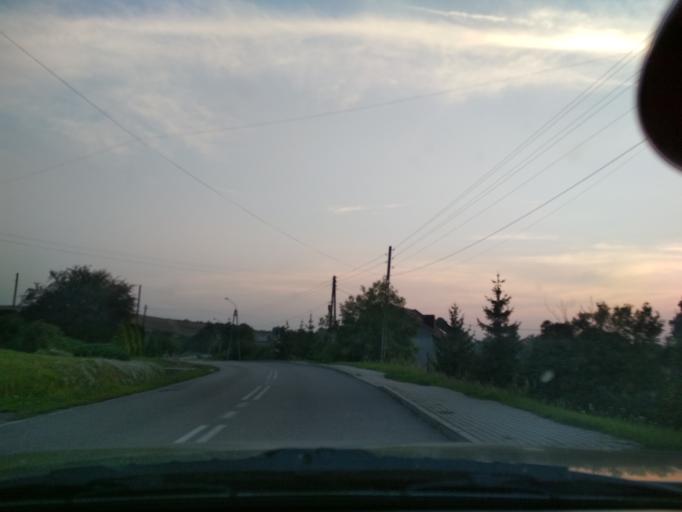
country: PL
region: Silesian Voivodeship
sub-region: Powiat zawiercianski
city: Pilica
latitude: 50.4678
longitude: 19.7148
